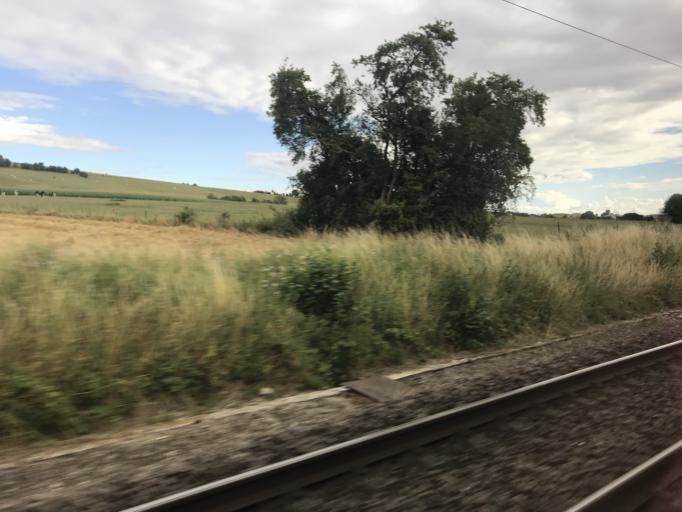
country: FR
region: Champagne-Ardenne
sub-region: Departement des Ardennes
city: Blagny
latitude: 49.5766
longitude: 5.2529
